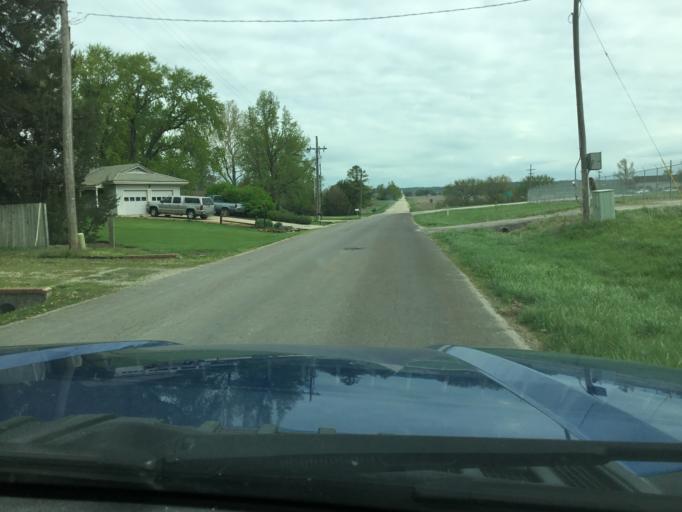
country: US
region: Kansas
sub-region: Douglas County
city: Lawrence
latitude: 39.0039
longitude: -95.2241
